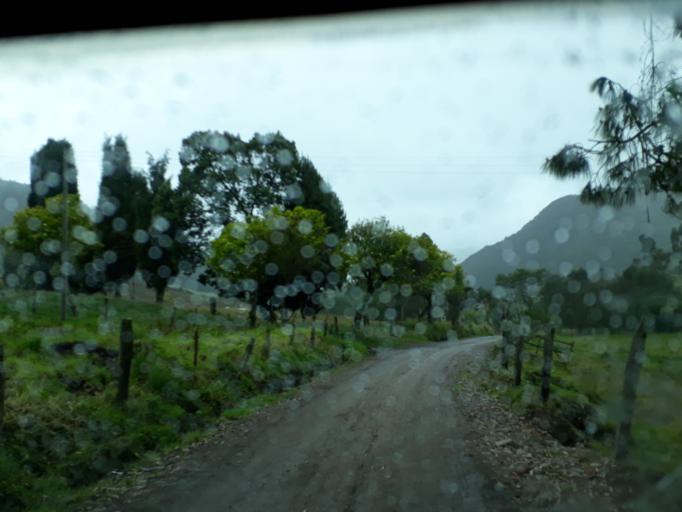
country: CO
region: Cundinamarca
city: Sutatausa
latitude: 5.1644
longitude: -73.9091
